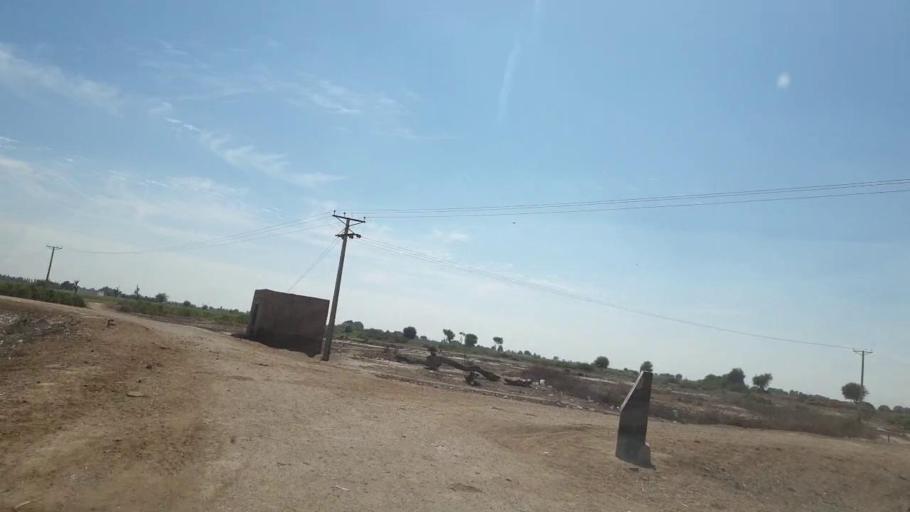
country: PK
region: Sindh
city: Pithoro
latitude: 25.6233
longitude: 69.2550
